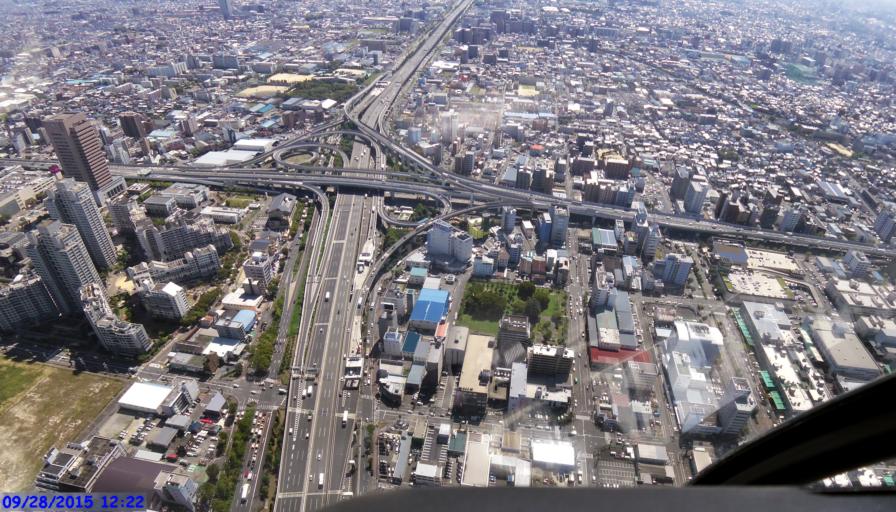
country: JP
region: Osaka
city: Daitocho
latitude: 34.6842
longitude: 135.5949
